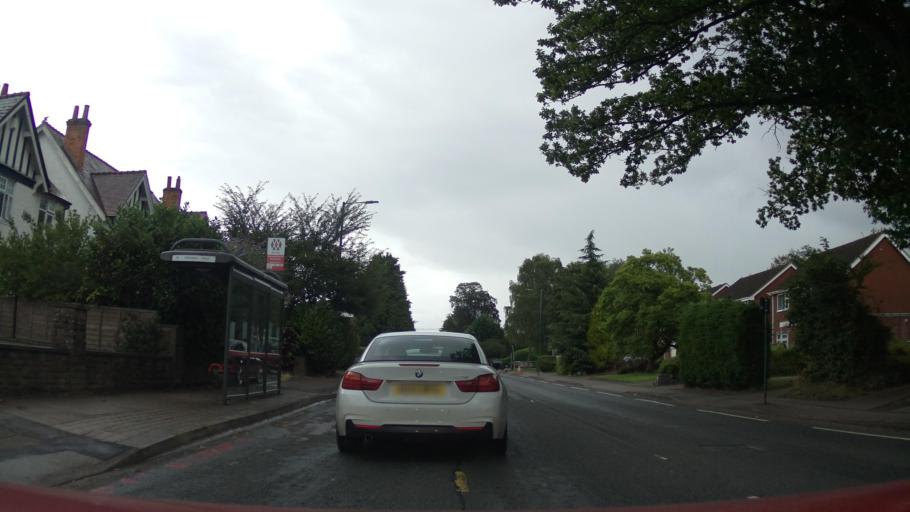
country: GB
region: England
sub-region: Solihull
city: Shirley
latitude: 52.4048
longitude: -1.8050
